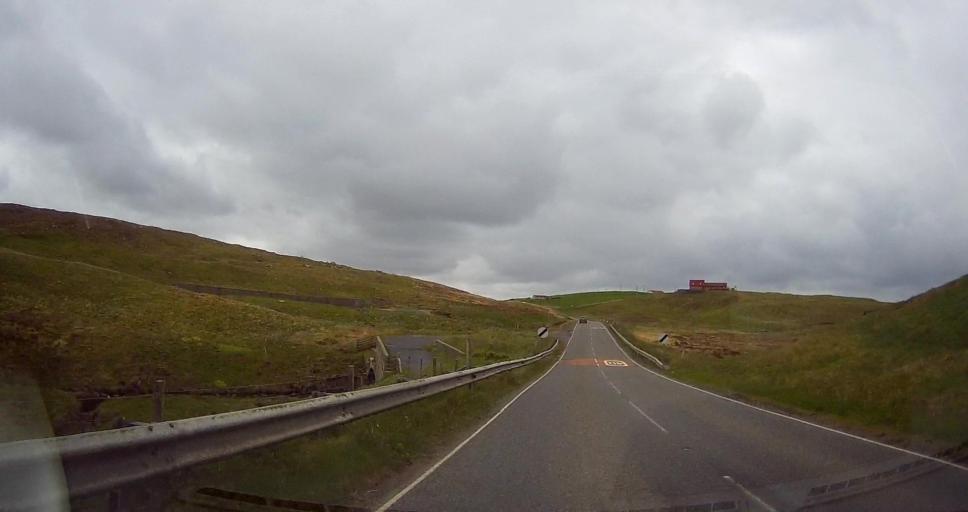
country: GB
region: Scotland
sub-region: Shetland Islands
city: Lerwick
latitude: 60.3854
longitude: -1.3423
